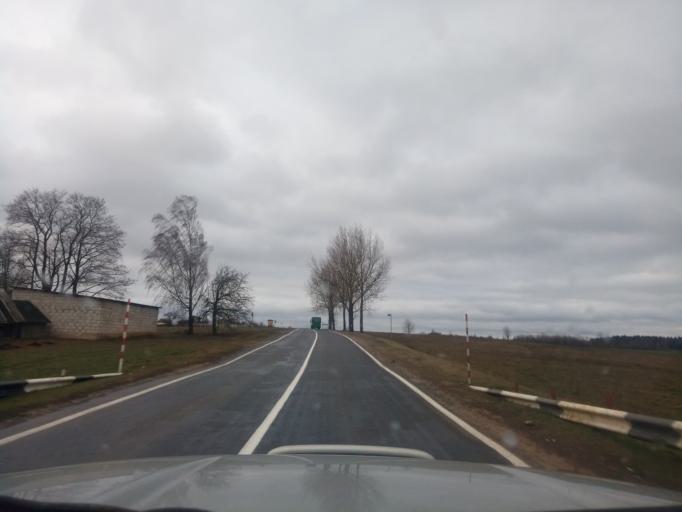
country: BY
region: Minsk
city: Kapyl'
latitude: 53.1779
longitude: 27.1671
